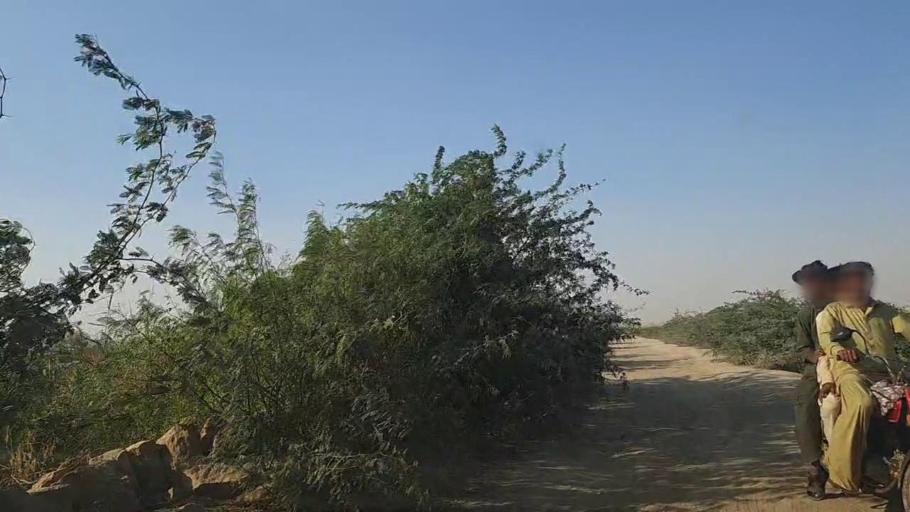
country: PK
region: Sindh
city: Daro Mehar
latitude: 25.0426
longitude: 68.1358
